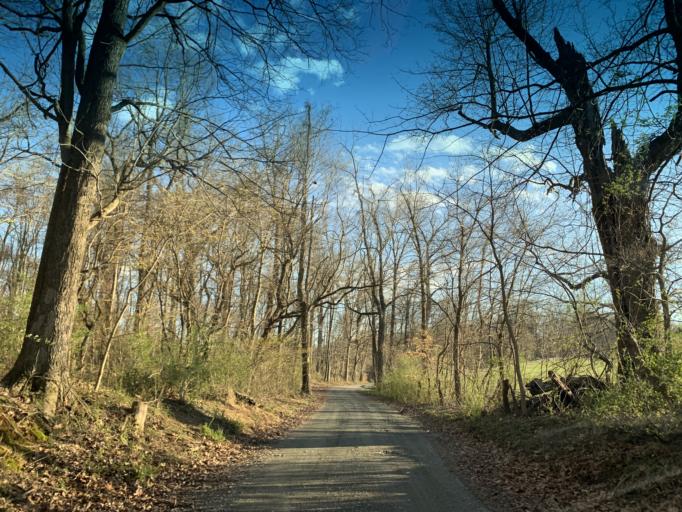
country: US
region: Maryland
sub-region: Harford County
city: Aberdeen
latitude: 39.6119
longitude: -76.2199
